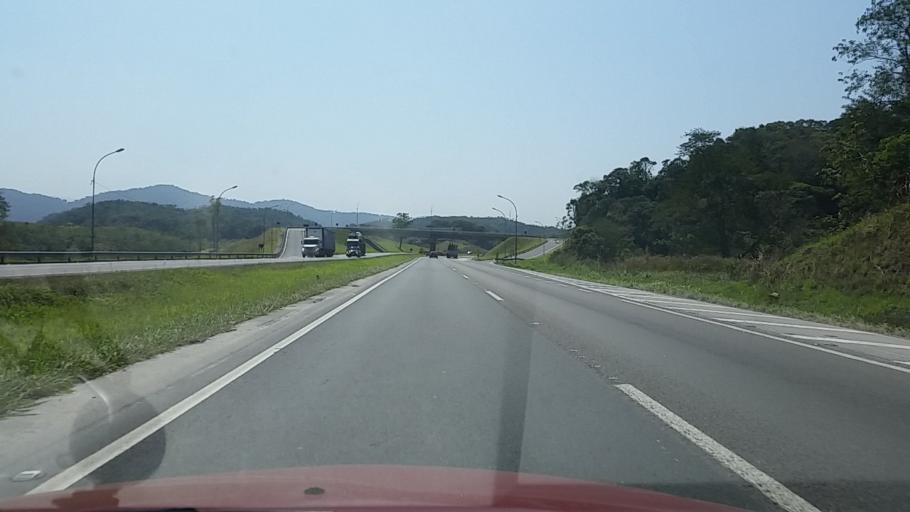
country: BR
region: Sao Paulo
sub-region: Miracatu
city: Miracatu
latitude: -24.2972
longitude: -47.4816
